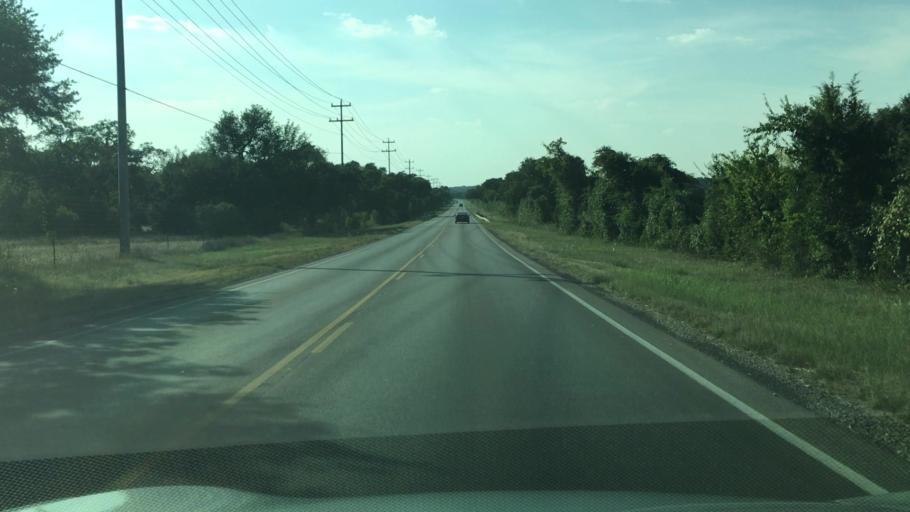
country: US
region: Texas
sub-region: Travis County
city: Shady Hollow
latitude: 30.1052
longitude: -97.9417
